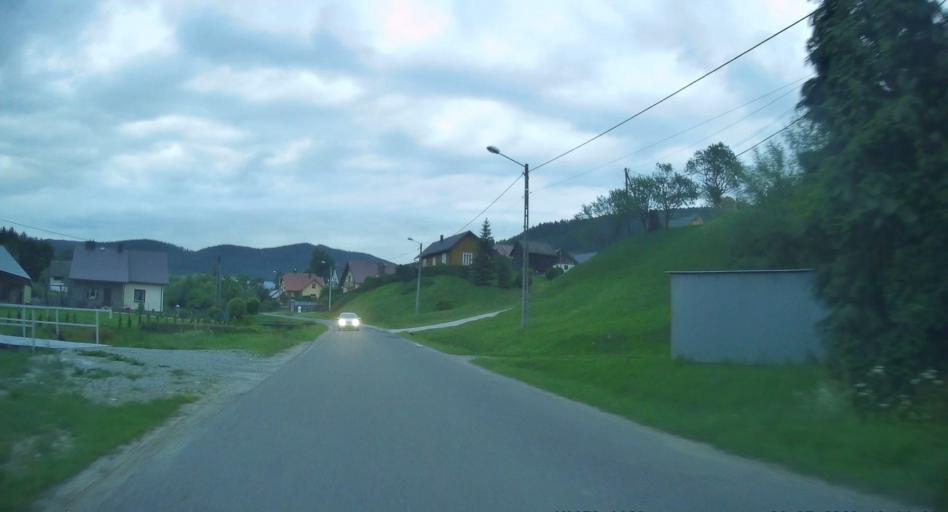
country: PL
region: Lesser Poland Voivodeship
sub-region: Powiat nowosadecki
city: Muszyna
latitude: 49.3815
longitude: 20.9223
